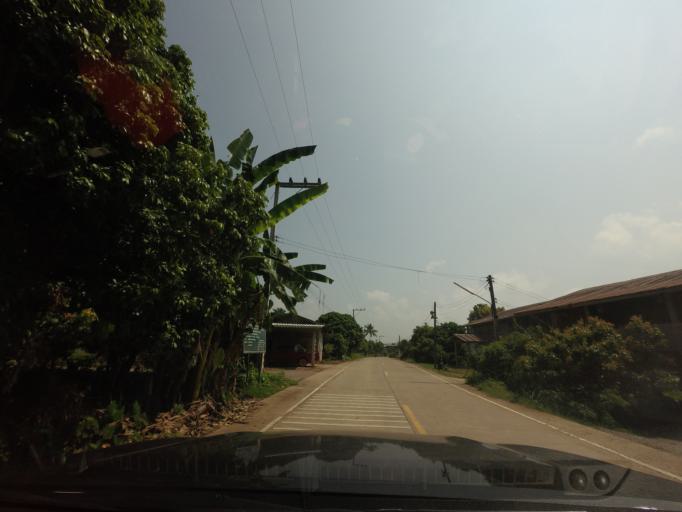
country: TH
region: Nan
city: Nan
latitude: 18.8608
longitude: 100.8112
